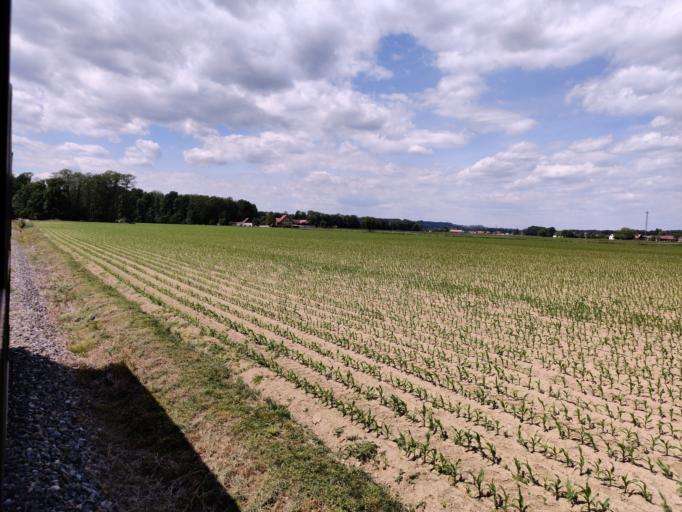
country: AT
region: Styria
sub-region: Politischer Bezirk Suedoststeiermark
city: Halbenrain
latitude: 46.7328
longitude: 15.9161
